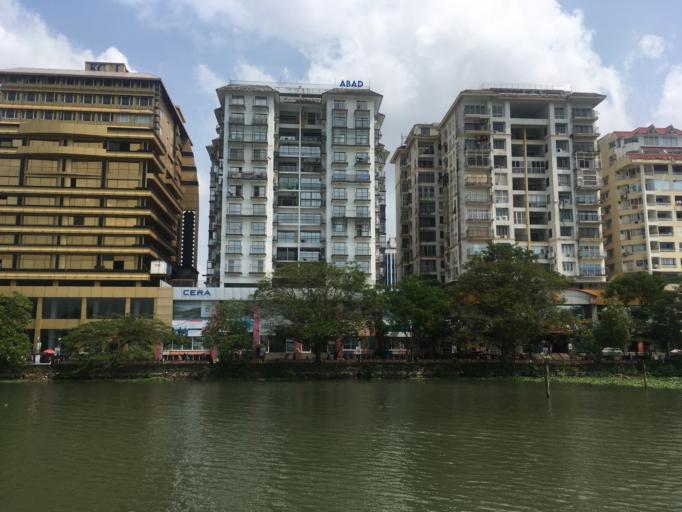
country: IN
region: Kerala
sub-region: Ernakulam
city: Cochin
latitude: 9.9771
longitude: 76.2757
